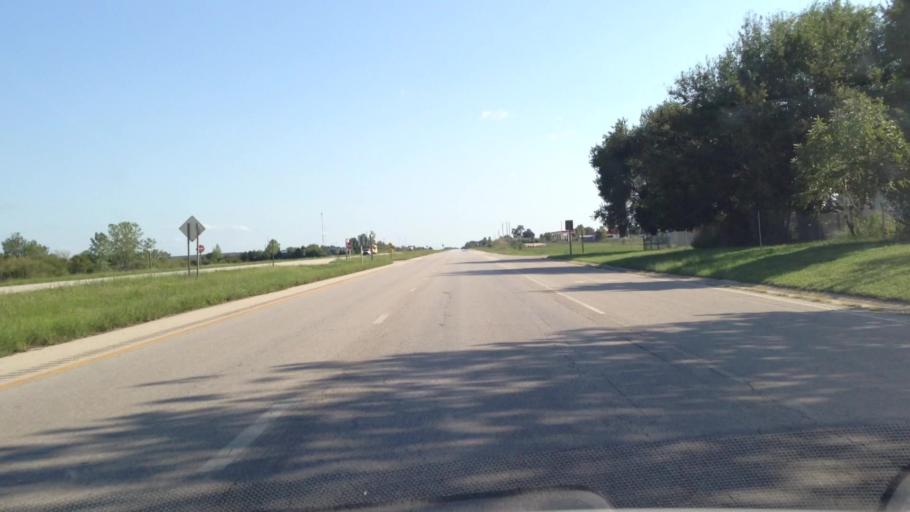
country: US
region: Kansas
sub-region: Bourbon County
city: Fort Scott
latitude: 37.8025
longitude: -94.7053
